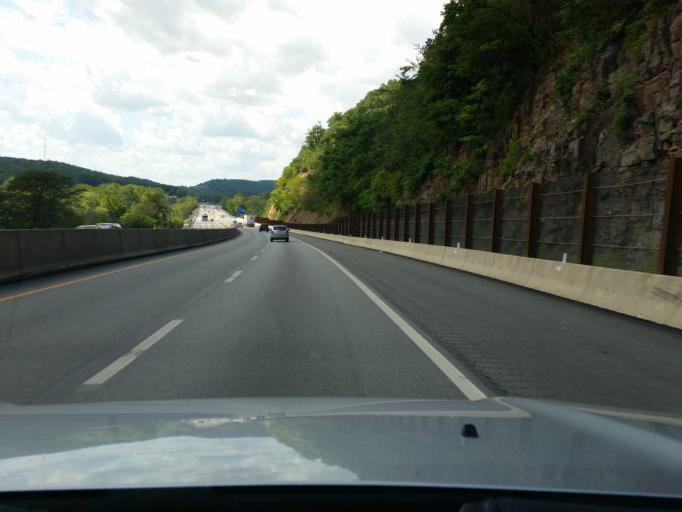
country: US
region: Pennsylvania
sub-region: Bedford County
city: Bedford
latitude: 40.0168
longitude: -78.4724
